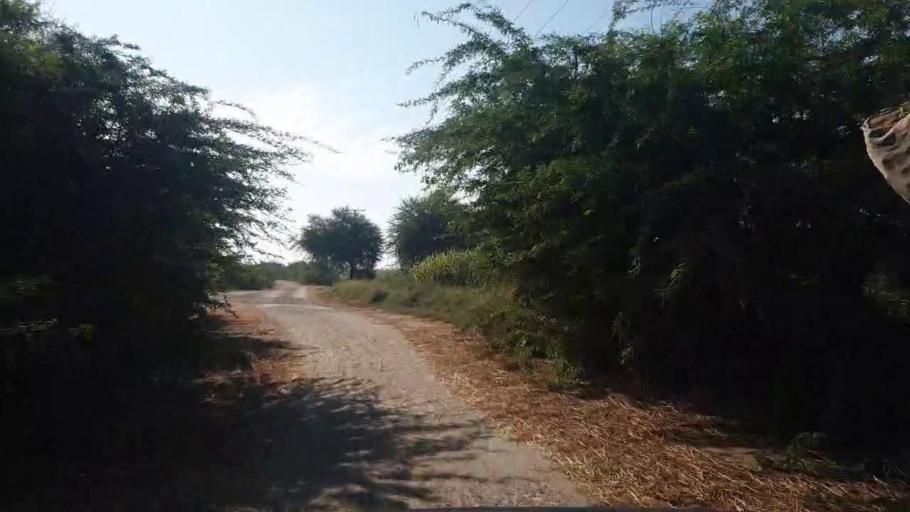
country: PK
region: Sindh
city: Talhar
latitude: 24.9441
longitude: 68.7935
